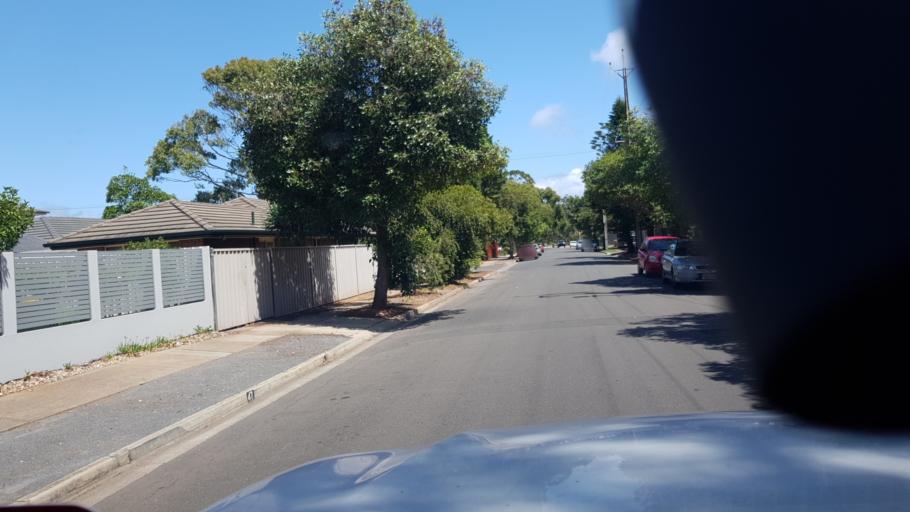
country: AU
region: South Australia
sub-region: Holdfast Bay
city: North Brighton
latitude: -35.0076
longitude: 138.5303
